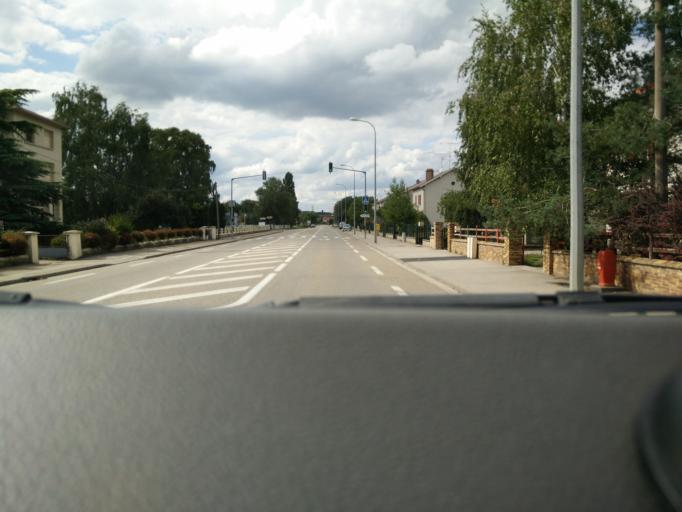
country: FR
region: Lorraine
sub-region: Departement de Meurthe-et-Moselle
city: Art-sur-Meurthe
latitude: 48.6418
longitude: 6.2622
